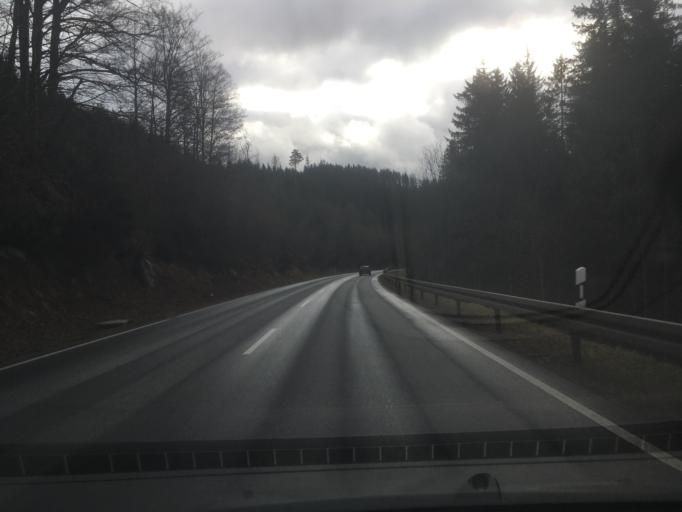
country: DE
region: Baden-Wuerttemberg
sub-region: Freiburg Region
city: Schluchsee
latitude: 47.7928
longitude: 8.1823
